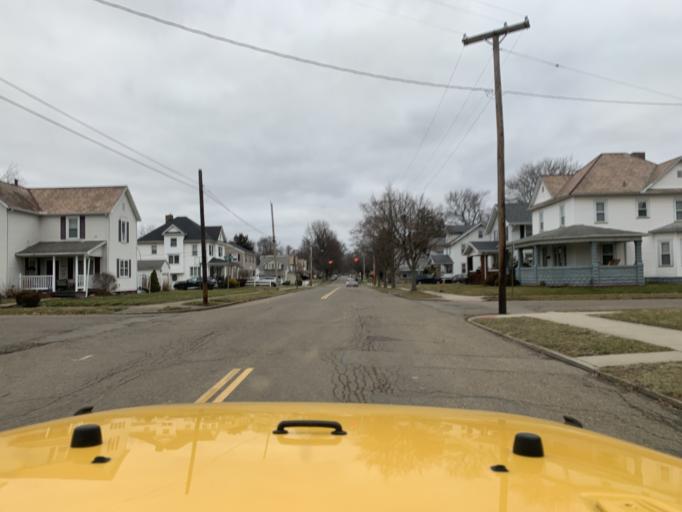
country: US
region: Ohio
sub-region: Tuscarawas County
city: Dover
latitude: 40.5276
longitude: -81.4789
